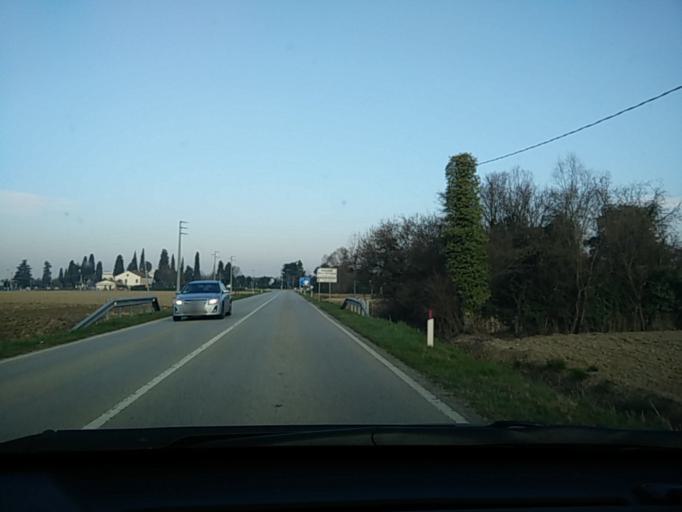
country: IT
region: Veneto
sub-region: Provincia di Treviso
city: Ponte di Piave
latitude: 45.7021
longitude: 12.4391
